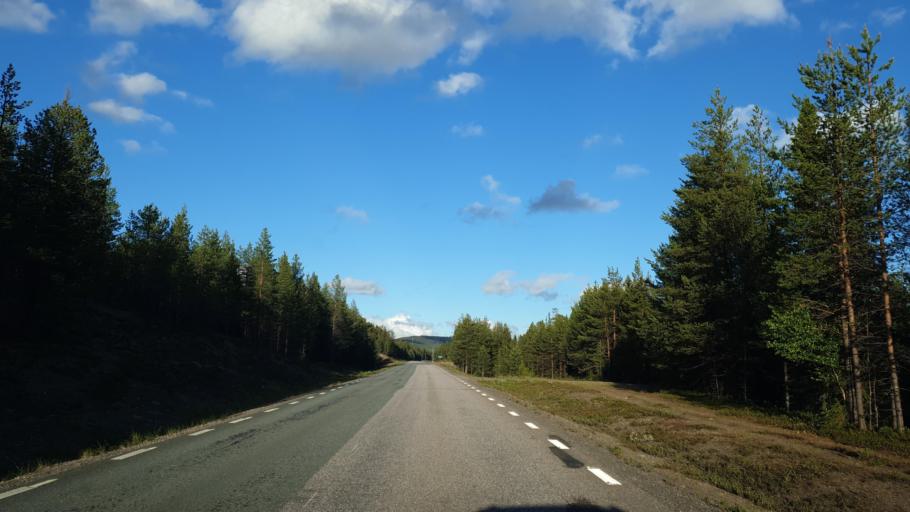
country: SE
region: Norrbotten
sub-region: Arvidsjaurs Kommun
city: Arvidsjaur
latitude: 65.7307
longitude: 18.6502
